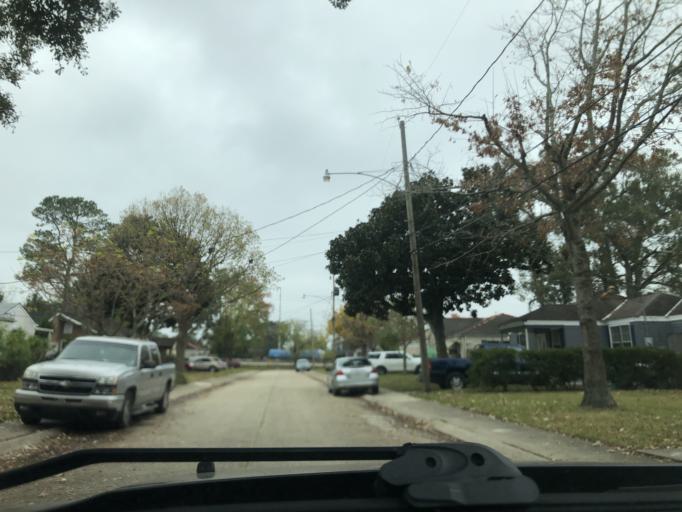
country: US
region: Louisiana
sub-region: Jefferson Parish
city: Metairie Terrace
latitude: 29.9726
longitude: -90.1658
